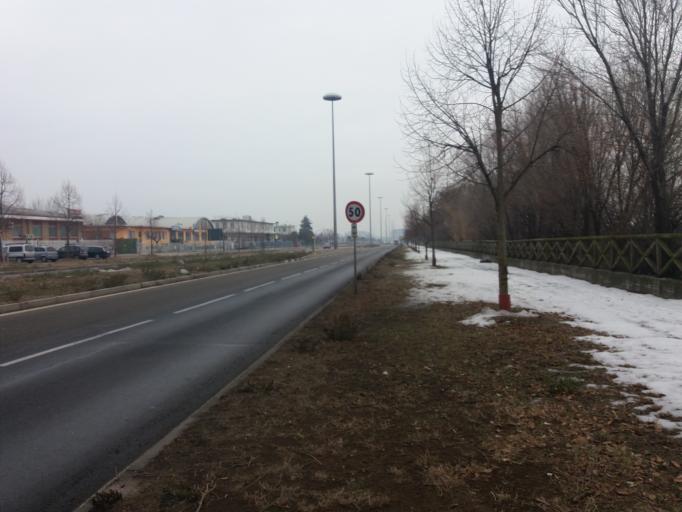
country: IT
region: Piedmont
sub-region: Provincia di Torino
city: Fornaci
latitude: 45.0406
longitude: 7.5955
